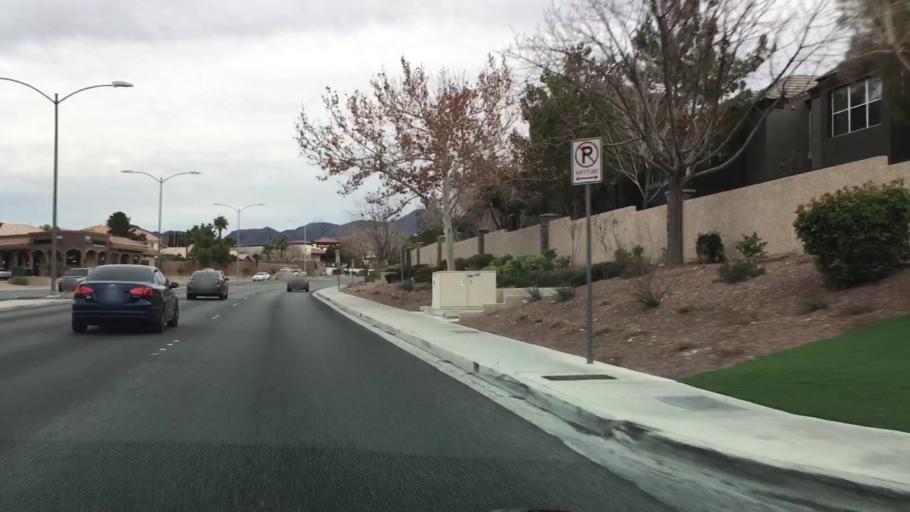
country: US
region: Nevada
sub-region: Clark County
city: Whitney
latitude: 35.9972
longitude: -115.1024
